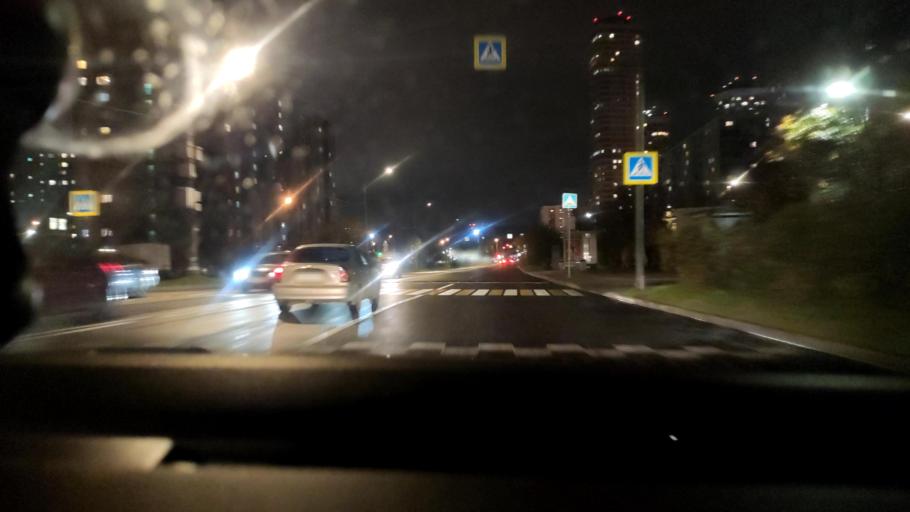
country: RU
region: Moscow
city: Strogino
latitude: 55.8076
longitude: 37.4182
